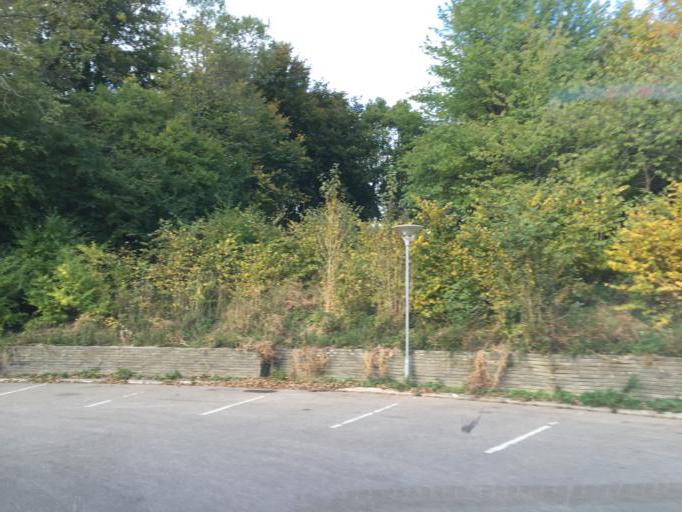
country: DK
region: Zealand
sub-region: Odsherred Kommune
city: Asnaes
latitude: 55.8142
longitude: 11.5010
